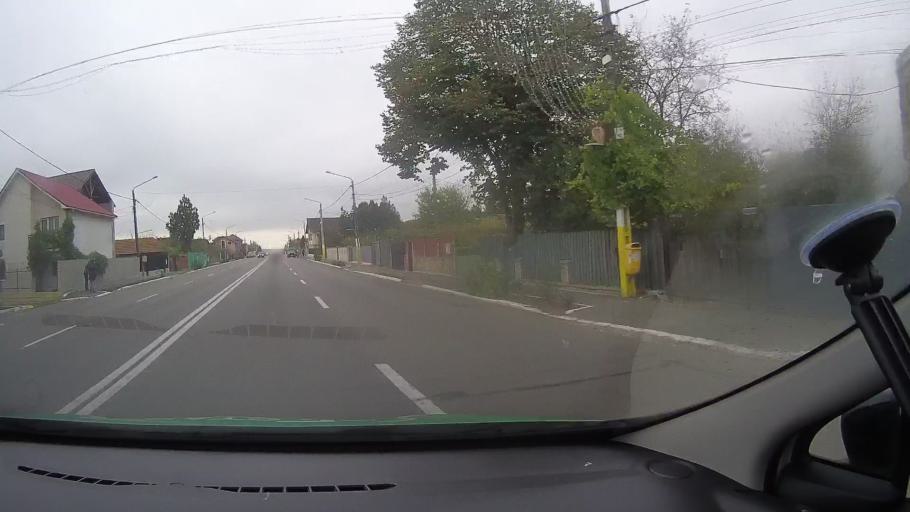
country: RO
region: Constanta
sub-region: Comuna Valu lui Traian
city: Valu lui Traian
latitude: 44.1673
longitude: 28.4545
